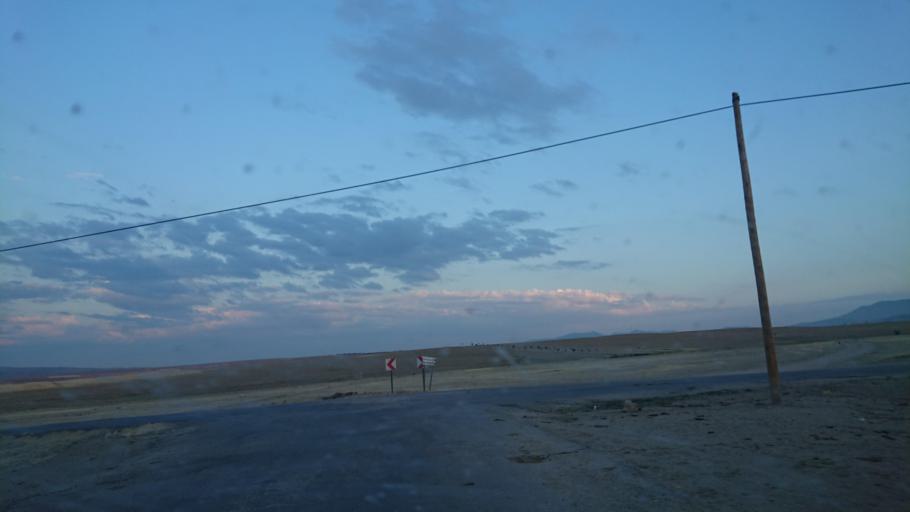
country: TR
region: Aksaray
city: Balci
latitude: 38.8236
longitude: 34.1006
